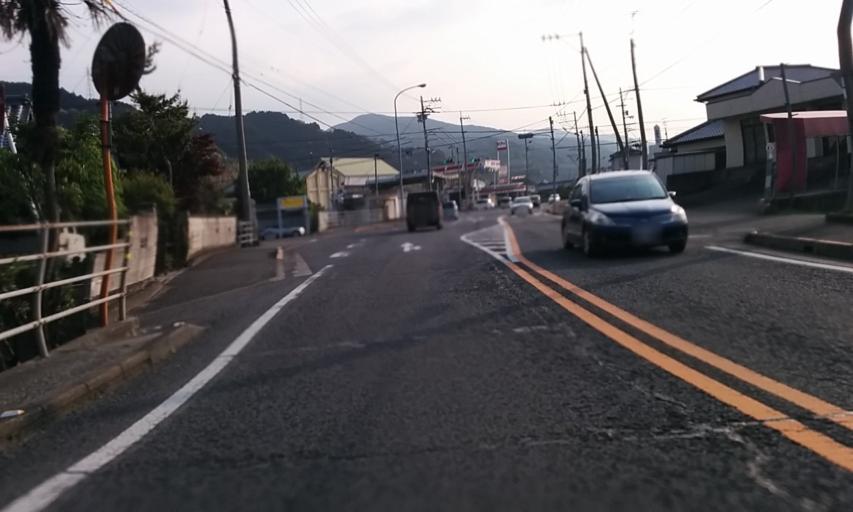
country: JP
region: Ehime
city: Saijo
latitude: 33.9004
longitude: 133.1816
